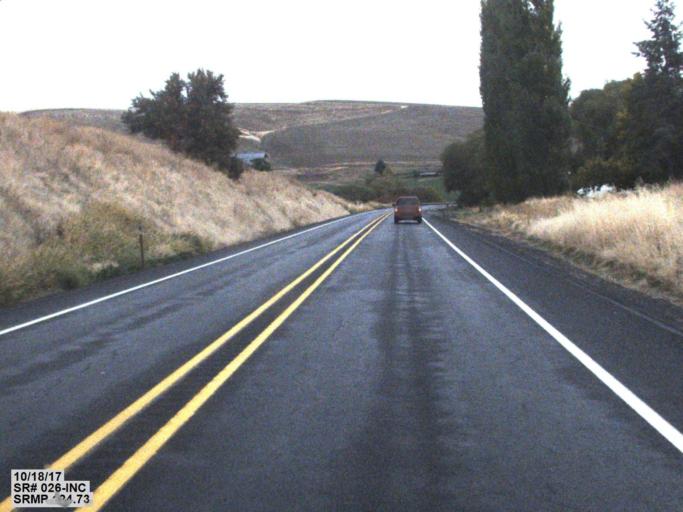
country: US
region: Washington
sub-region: Whitman County
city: Colfax
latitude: 46.8310
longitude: -117.5142
